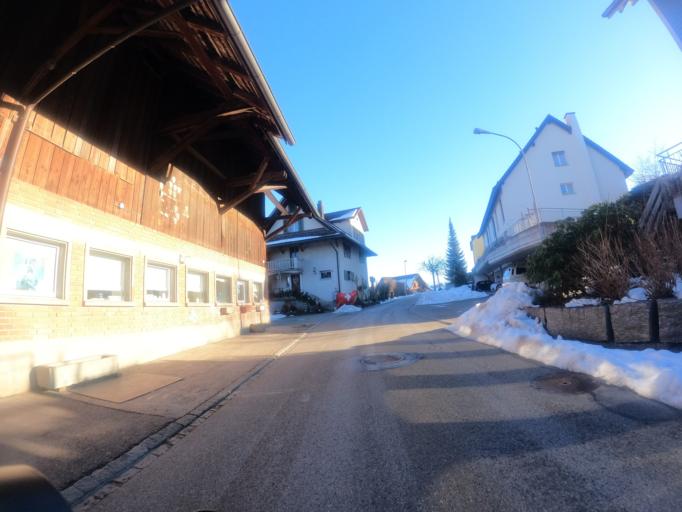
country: CH
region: Zurich
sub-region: Bezirk Affoltern
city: Hedingen
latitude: 47.2888
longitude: 8.4388
